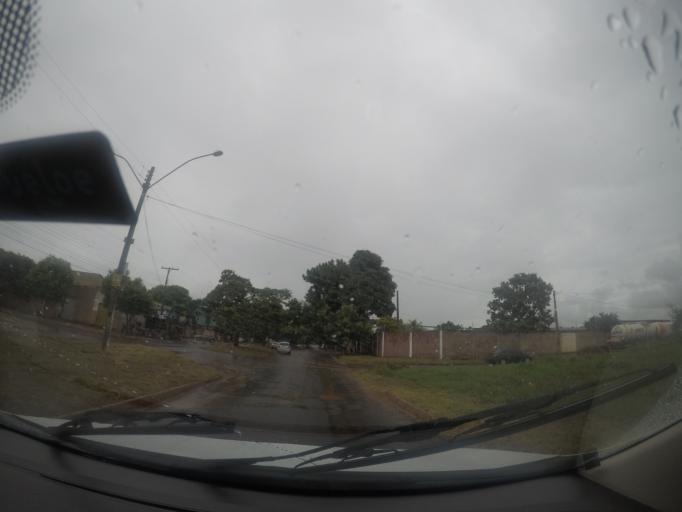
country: BR
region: Goias
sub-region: Trindade
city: Trindade
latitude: -16.6433
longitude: -49.4347
